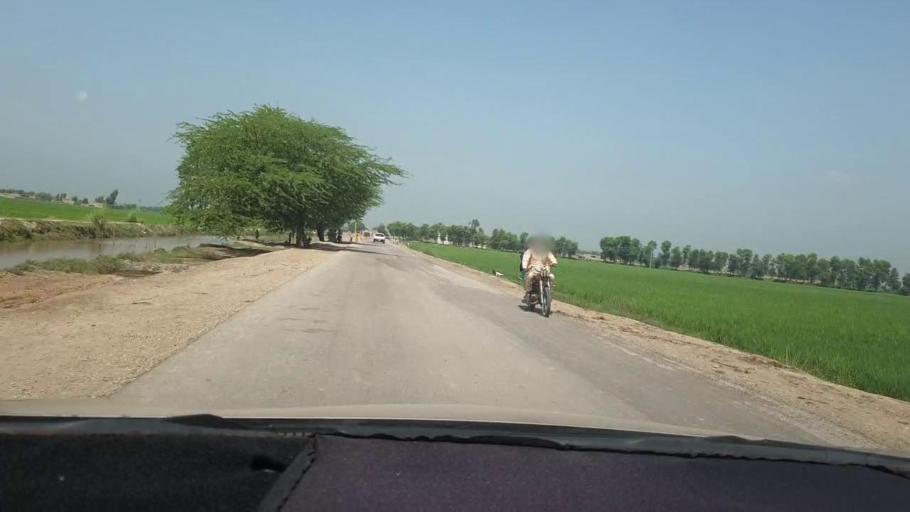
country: PK
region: Sindh
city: Miro Khan
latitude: 27.7695
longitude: 68.0659
